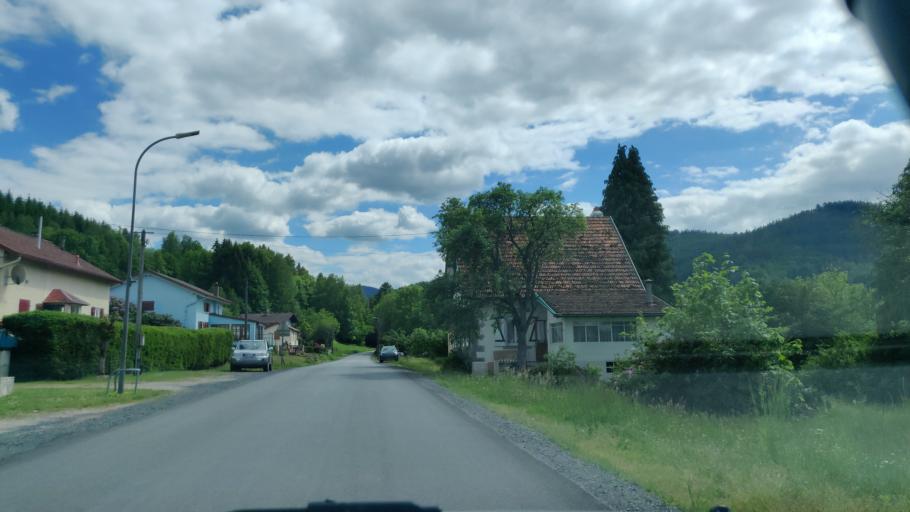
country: FR
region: Lorraine
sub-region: Departement des Vosges
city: Fraize
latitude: 48.1824
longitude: 6.9735
